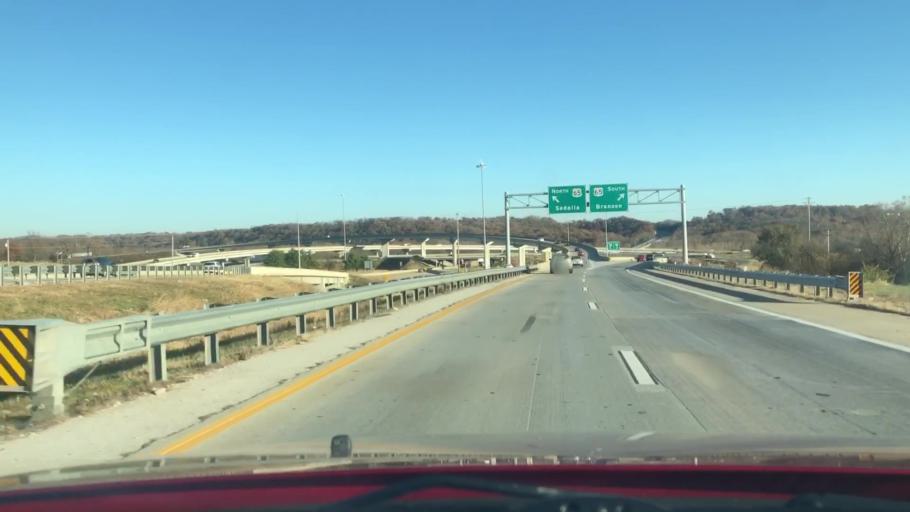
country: US
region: Missouri
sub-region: Christian County
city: Nixa
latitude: 37.1297
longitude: -93.2364
